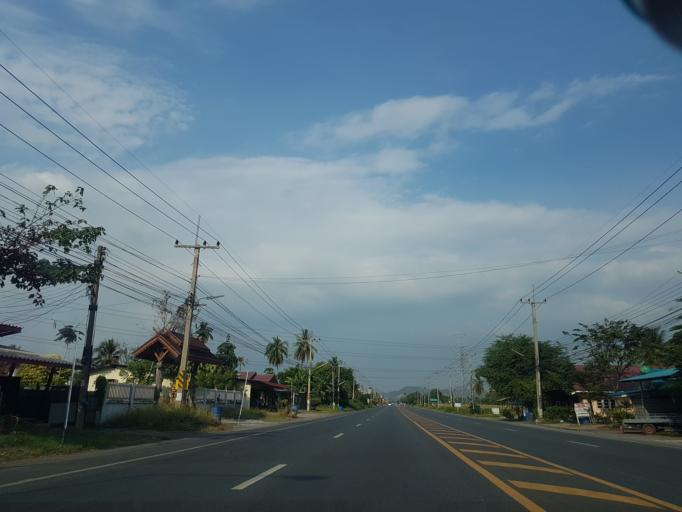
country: TH
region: Sara Buri
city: Ban Mo
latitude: 14.6428
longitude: 100.7572
